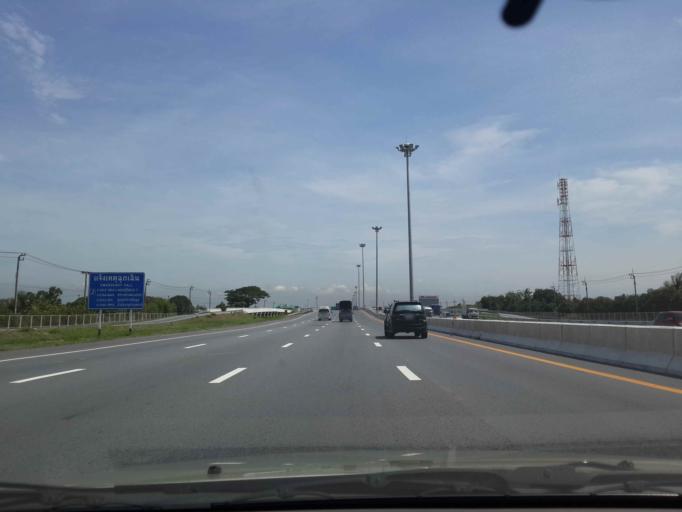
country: TH
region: Bangkok
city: Lat Krabang
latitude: 13.6952
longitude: 100.8274
